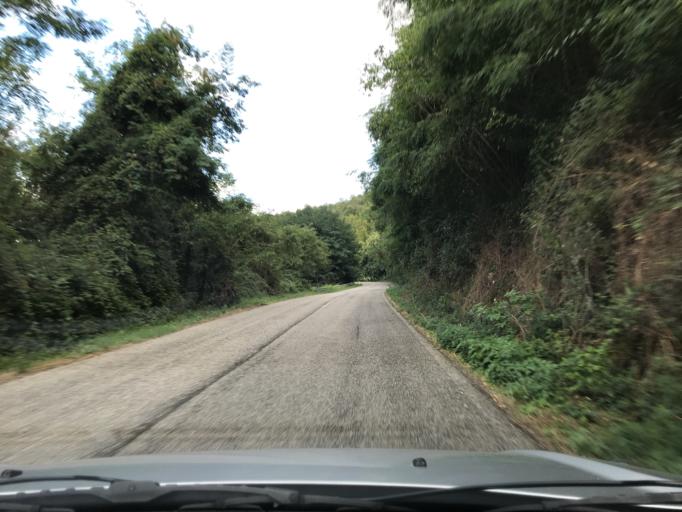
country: IT
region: Umbria
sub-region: Provincia di Terni
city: Guardea
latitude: 42.6561
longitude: 12.3419
